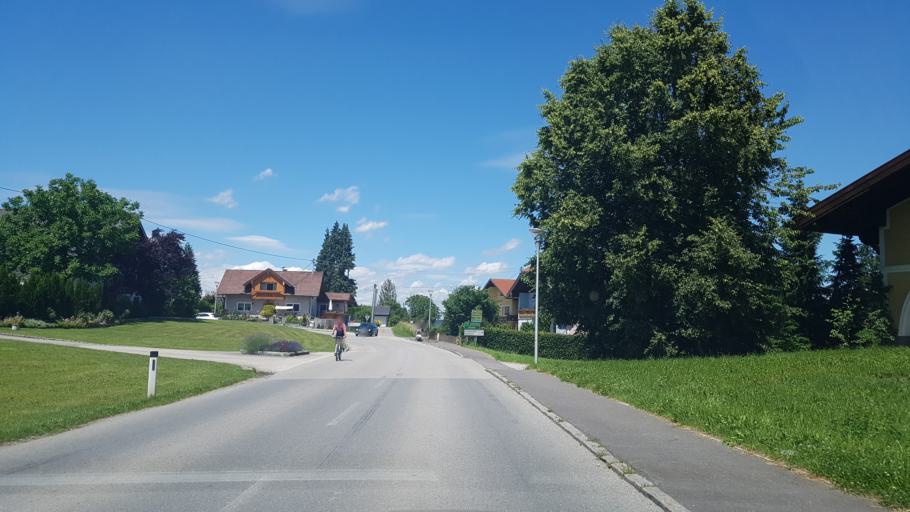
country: AT
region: Salzburg
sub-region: Politischer Bezirk Salzburg-Umgebung
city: Strasswalchen
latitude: 48.0079
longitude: 13.2157
